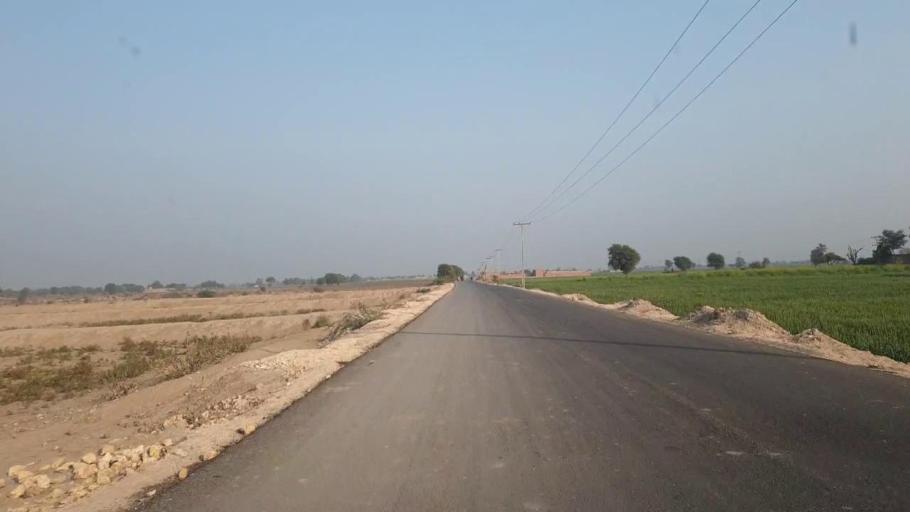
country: PK
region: Sindh
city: Hala
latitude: 25.8112
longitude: 68.4408
